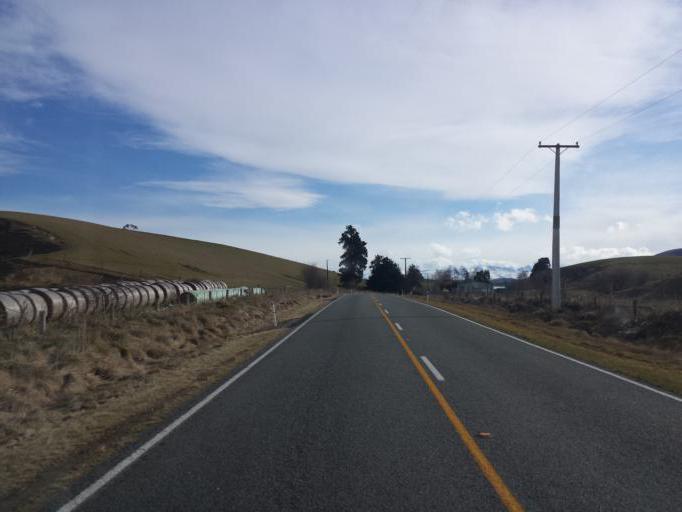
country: NZ
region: Canterbury
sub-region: Timaru District
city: Pleasant Point
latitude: -44.1096
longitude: 171.0110
